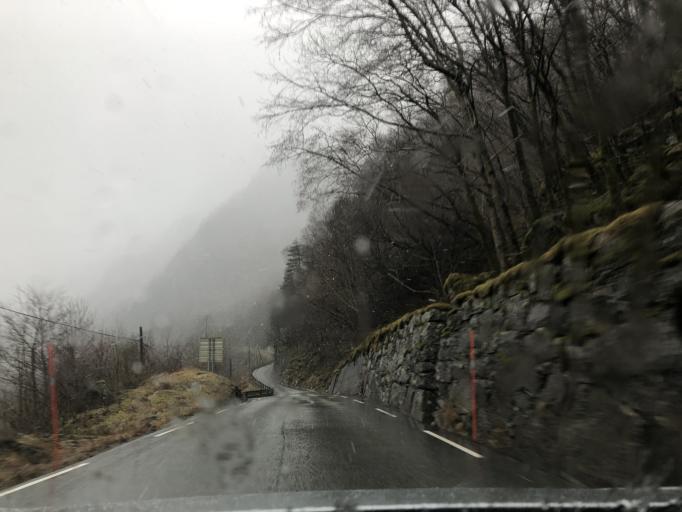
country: NO
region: Rogaland
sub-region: Suldal
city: Sand
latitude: 59.4070
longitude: 6.2076
